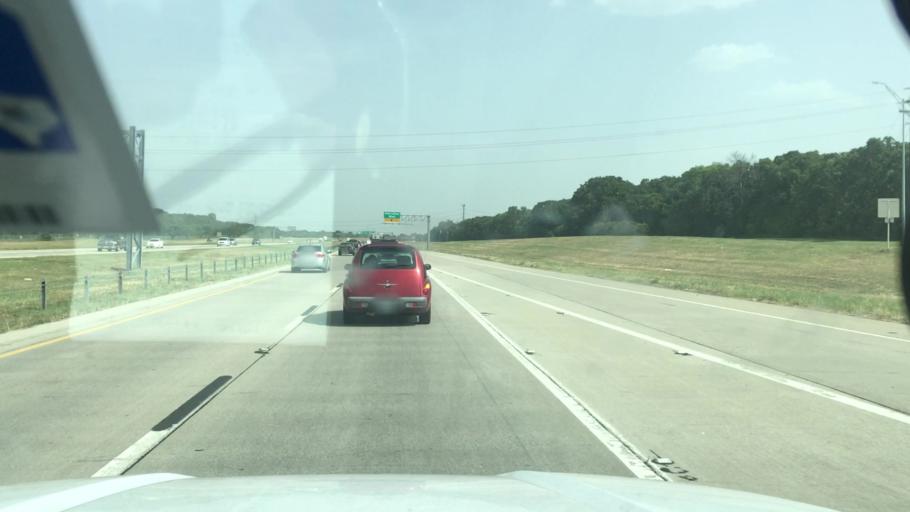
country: US
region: Texas
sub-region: Tarrant County
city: Euless
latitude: 32.8772
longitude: -97.0734
